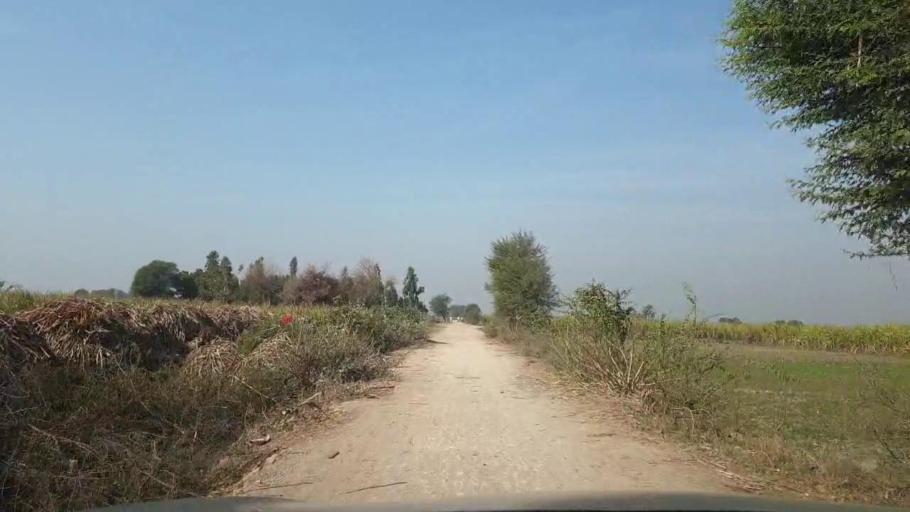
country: PK
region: Sindh
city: Tando Allahyar
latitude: 25.6022
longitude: 68.7173
